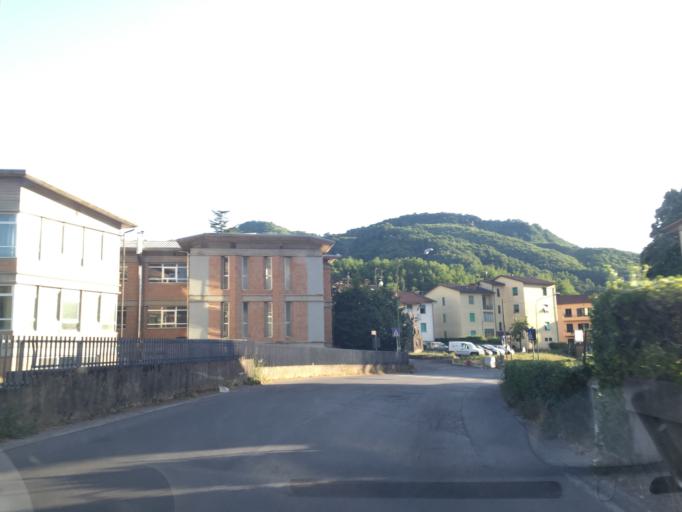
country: IT
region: Tuscany
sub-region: Provincia di Lucca
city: Castelnuovo di Garfagnana
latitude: 44.1044
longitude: 10.4078
